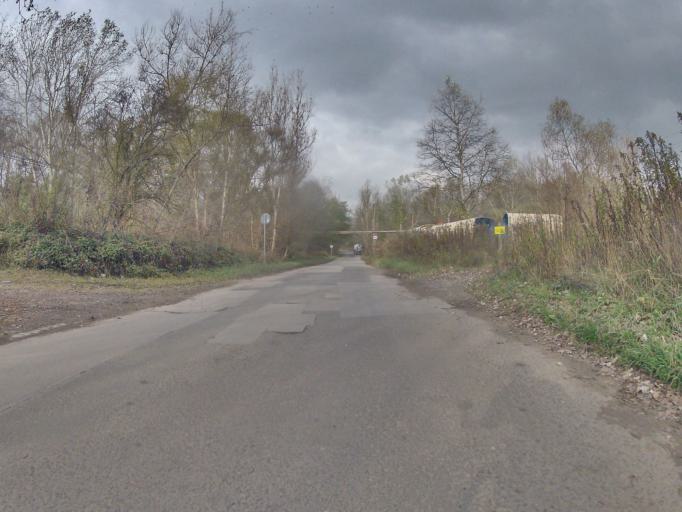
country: PL
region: Lesser Poland Voivodeship
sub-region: Powiat wielicki
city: Wegrzce Wielkie
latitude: 50.0639
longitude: 20.1025
